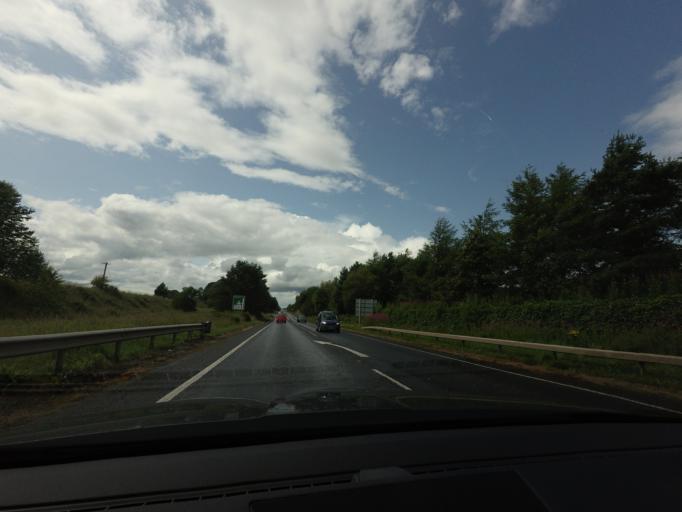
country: GB
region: Scotland
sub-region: Moray
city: Lhanbryd
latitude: 57.6332
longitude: -3.2194
